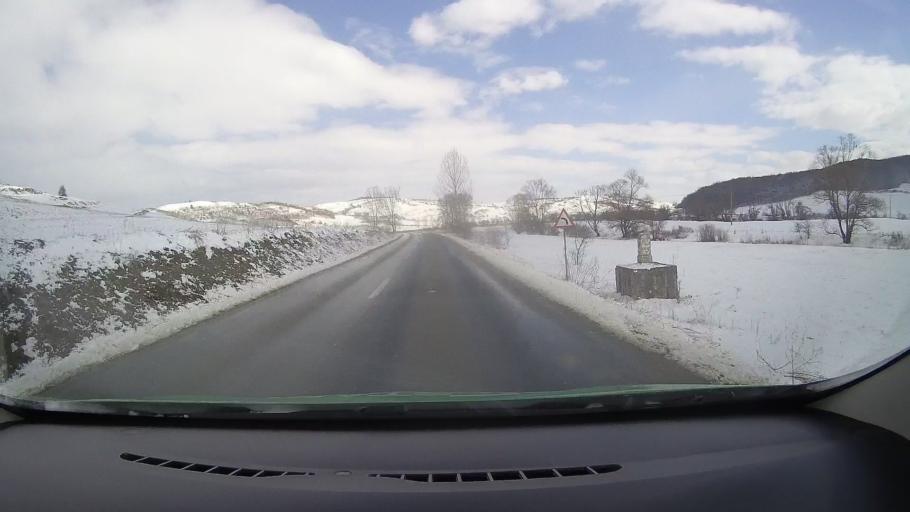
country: RO
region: Sibiu
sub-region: Comuna Altina
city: Altina
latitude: 45.9637
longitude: 24.4655
